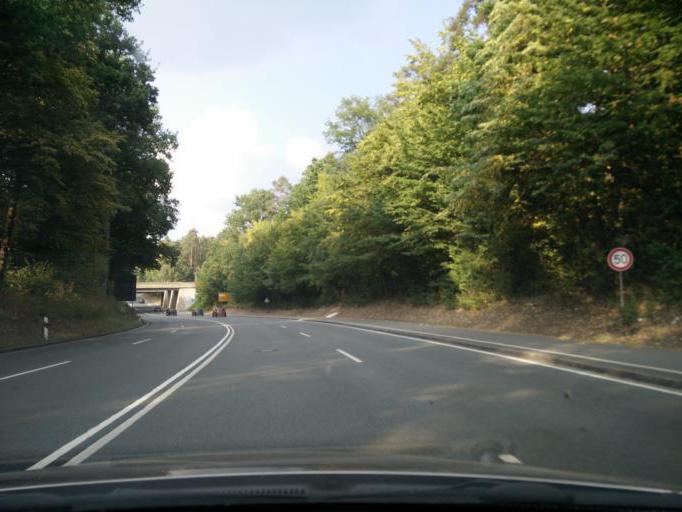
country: DE
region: Bavaria
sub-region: Regierungsbezirk Mittelfranken
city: Wendelstein
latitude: 49.4174
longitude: 11.1570
